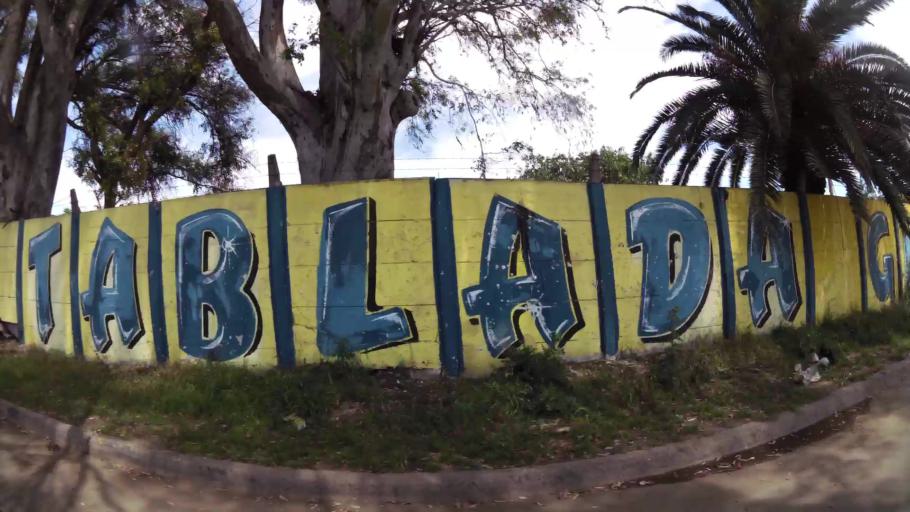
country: AR
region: Santa Fe
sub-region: Departamento de Rosario
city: Rosario
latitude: -32.9829
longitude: -60.6257
